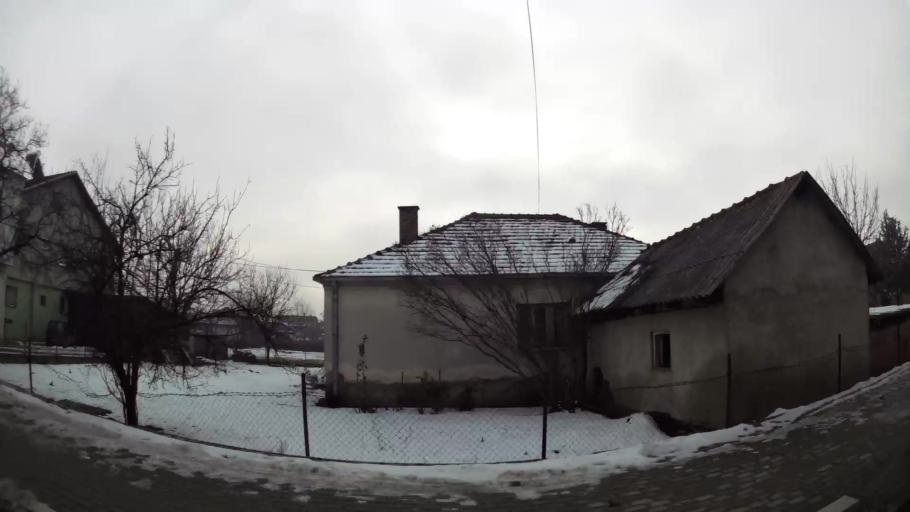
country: MK
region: Ilinden
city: Ilinden
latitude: 41.9949
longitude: 21.5722
